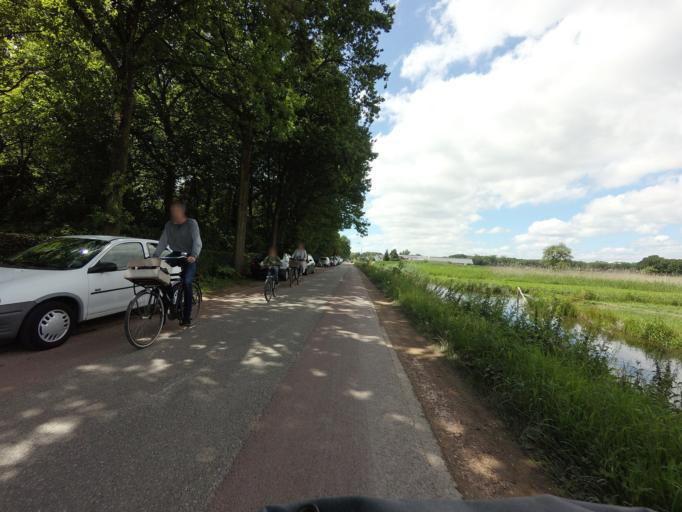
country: NL
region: Utrecht
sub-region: Gemeente Utrechtse Heuvelrug
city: Doorn
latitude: 52.0146
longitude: 5.3137
